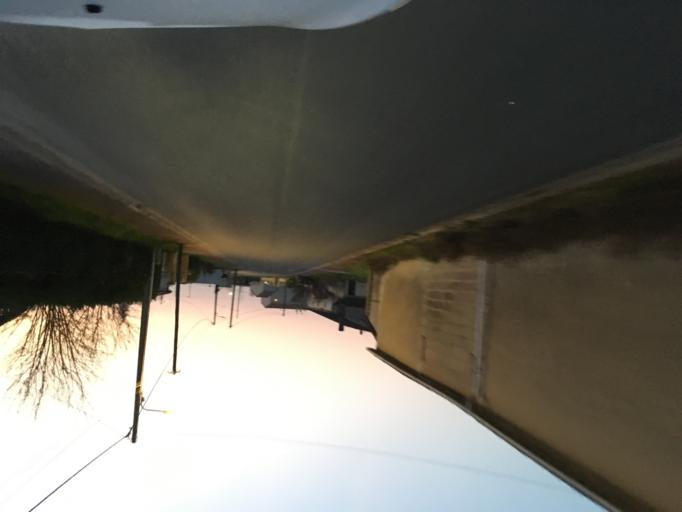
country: FR
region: Aquitaine
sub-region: Departement de la Gironde
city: Braud-et-Saint-Louis
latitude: 45.2486
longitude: -0.6321
